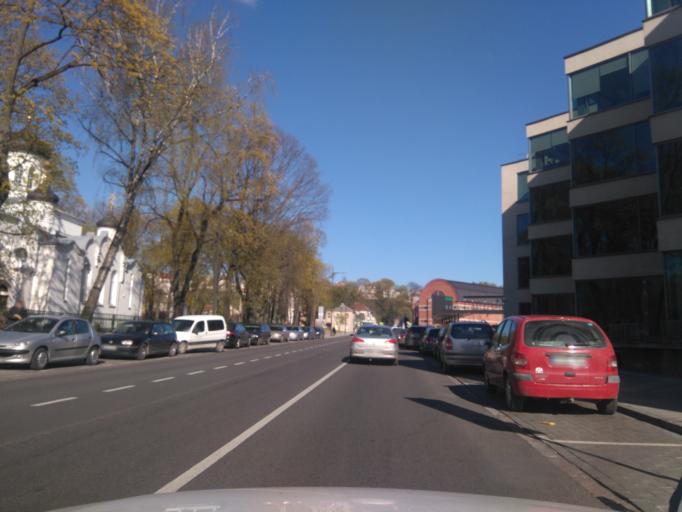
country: LT
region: Kauno apskritis
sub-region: Kaunas
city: Aleksotas
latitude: 54.8903
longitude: 23.9261
